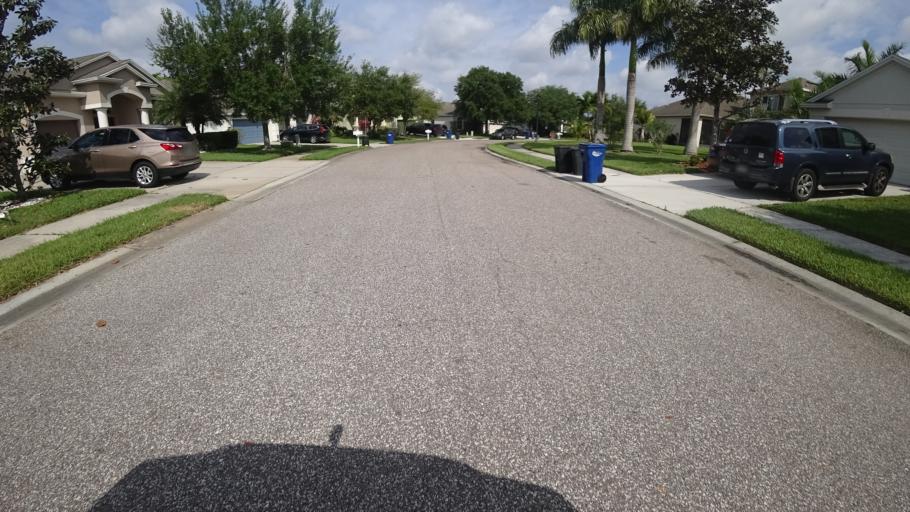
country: US
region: Florida
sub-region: Manatee County
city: Ellenton
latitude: 27.5656
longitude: -82.4663
